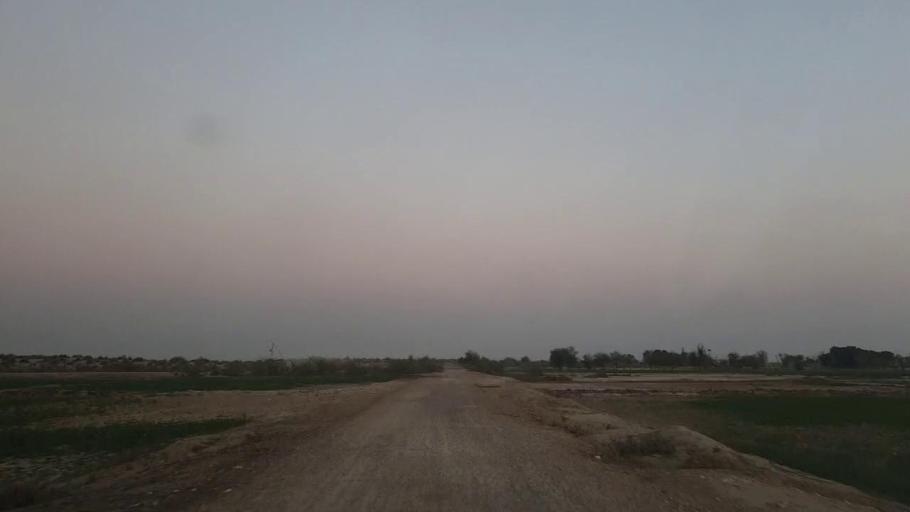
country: PK
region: Sindh
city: Bandhi
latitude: 26.6060
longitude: 68.3773
